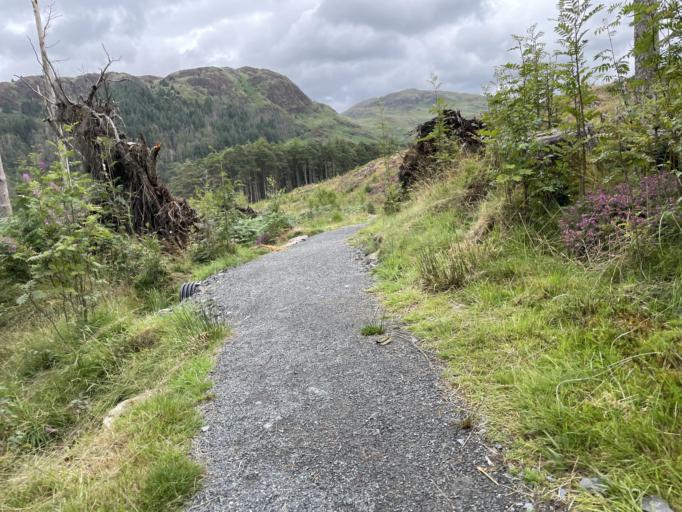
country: GB
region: Scotland
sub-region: Dumfries and Galloway
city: Newton Stewart
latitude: 55.0854
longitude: -4.4954
